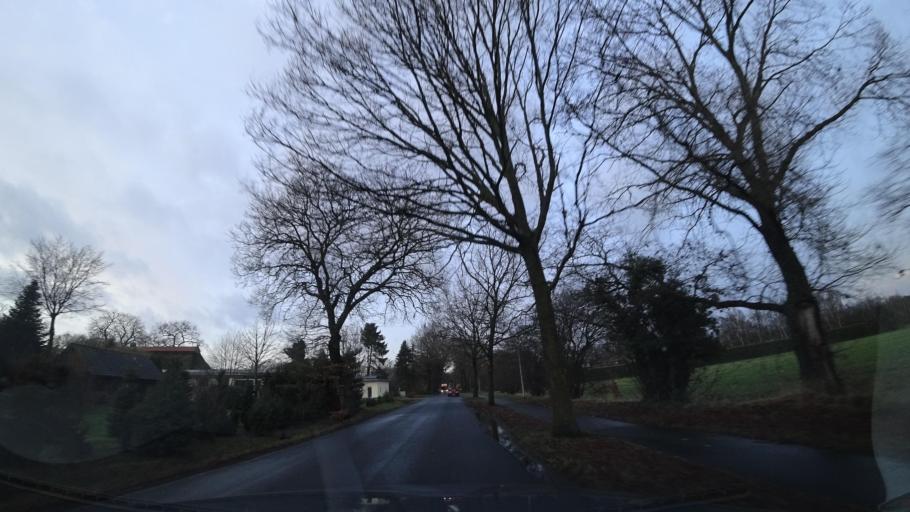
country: DE
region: Lower Saxony
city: Oldenburg
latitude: 53.1023
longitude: 8.2762
